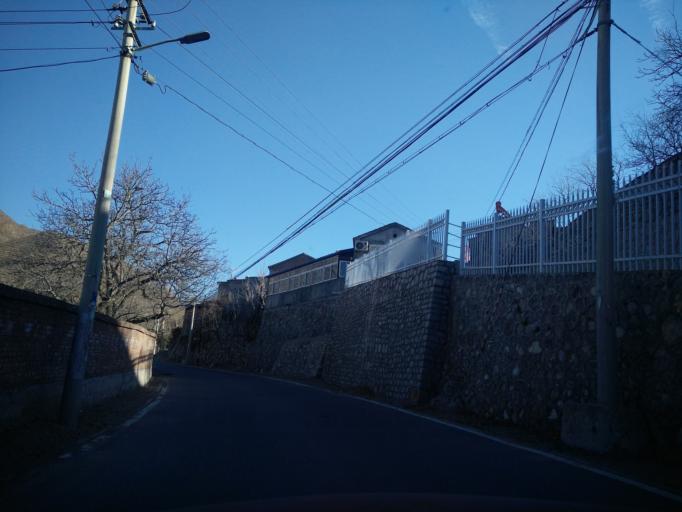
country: CN
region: Beijing
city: Zhaitang
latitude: 40.0675
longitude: 115.7162
